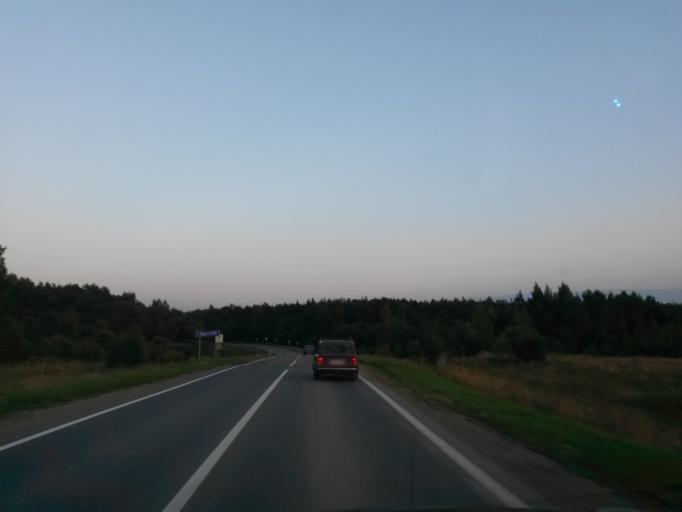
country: RU
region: Jaroslavl
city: Konstantinovskiy
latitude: 57.8608
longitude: 39.6133
